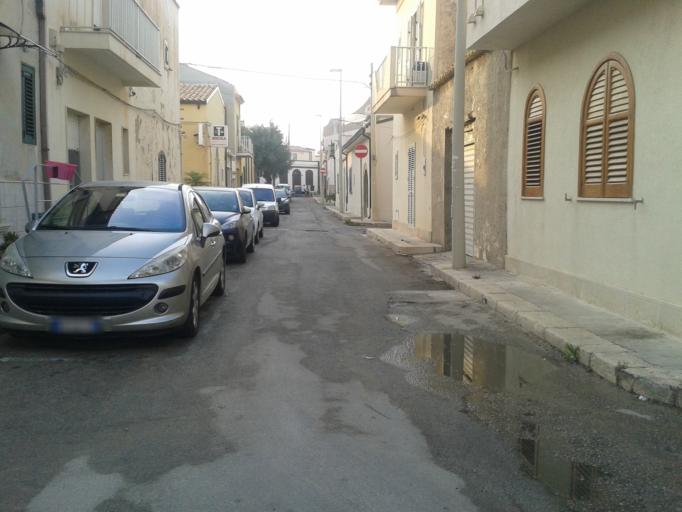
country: IT
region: Sicily
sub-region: Ragusa
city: Santa Croce Camerina
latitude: 36.7879
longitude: 14.4938
